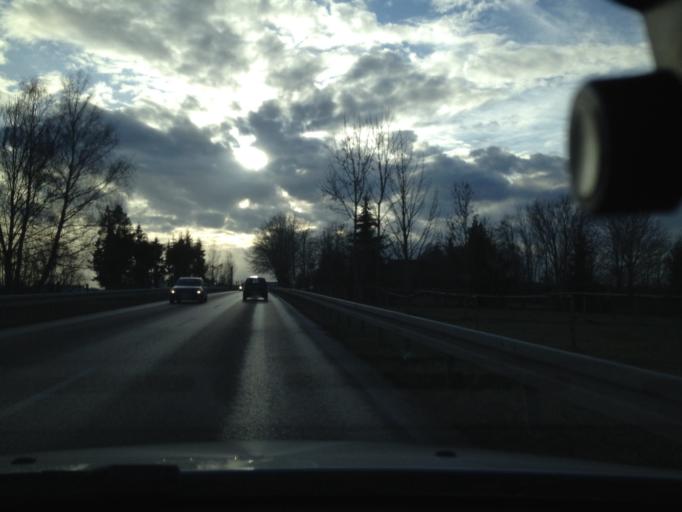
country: DE
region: Bavaria
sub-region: Swabia
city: Schwabmunchen
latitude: 48.2031
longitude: 10.7665
